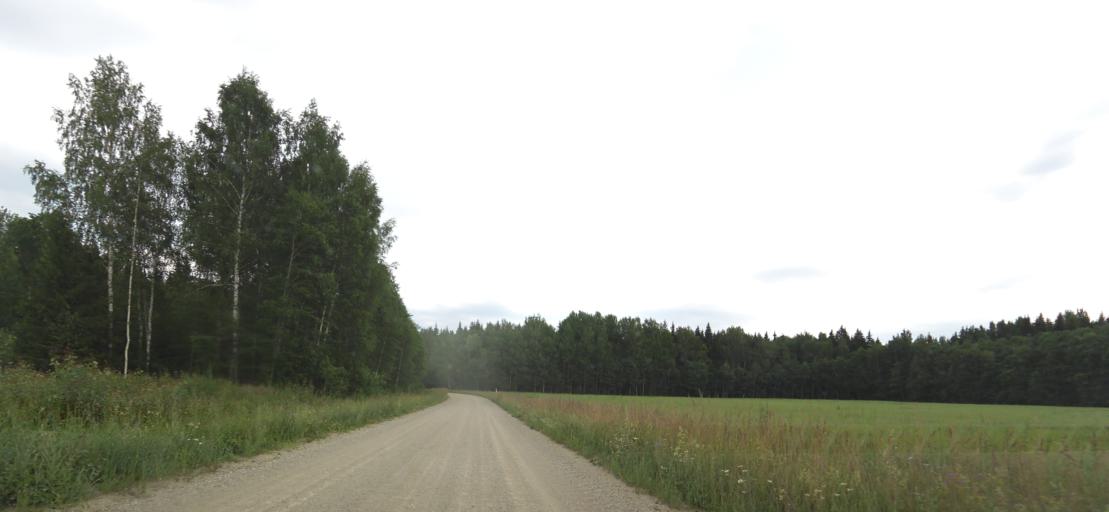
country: LT
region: Panevezys
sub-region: Birzai
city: Birzai
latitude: 56.2970
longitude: 24.9619
